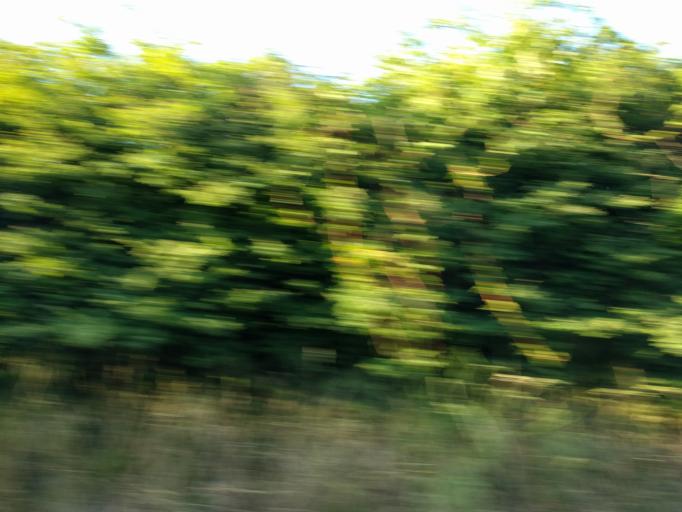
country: DK
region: South Denmark
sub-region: Kerteminde Kommune
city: Munkebo
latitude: 55.6077
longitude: 10.6191
